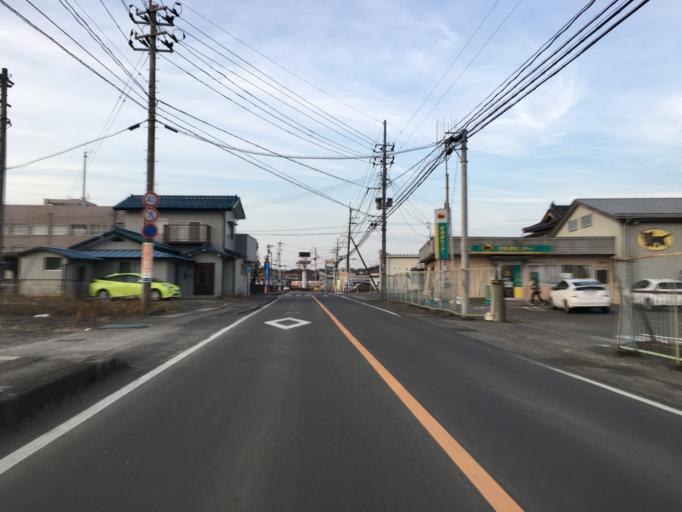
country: JP
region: Fukushima
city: Ishikawa
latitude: 37.0171
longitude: 140.3916
